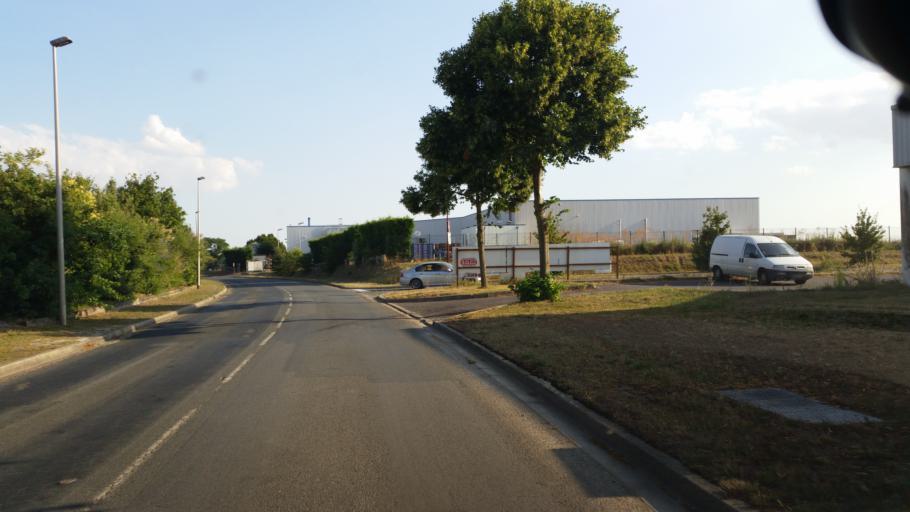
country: FR
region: Poitou-Charentes
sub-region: Departement de la Charente-Maritime
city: Marans
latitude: 46.3081
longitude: -1.0064
